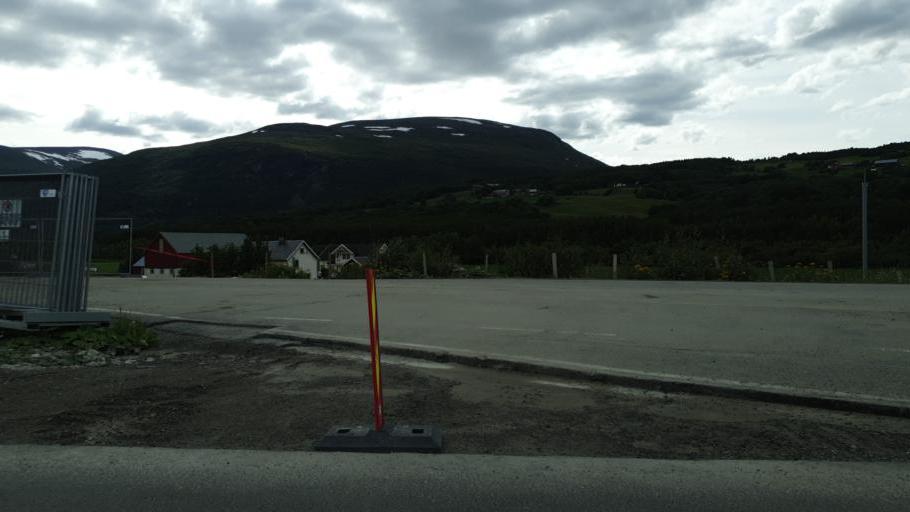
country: NO
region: Sor-Trondelag
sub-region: Oppdal
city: Oppdal
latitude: 62.5632
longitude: 9.6428
